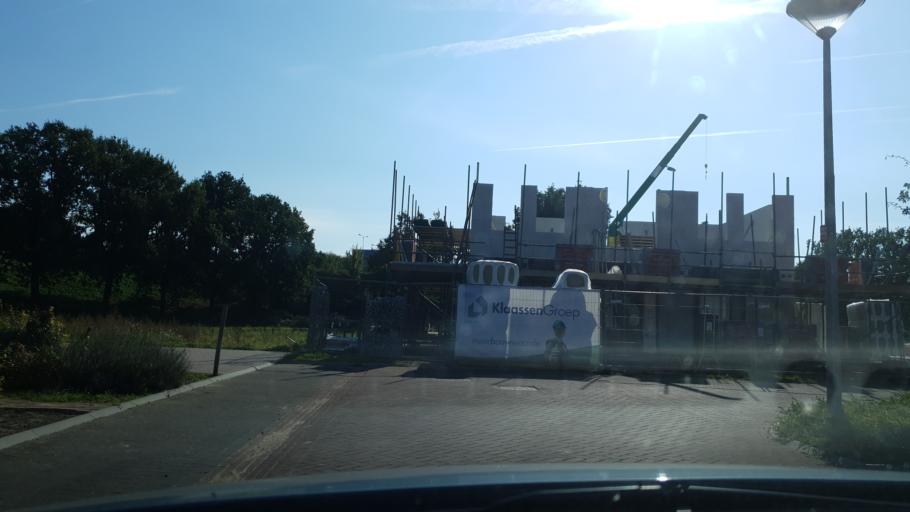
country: NL
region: Gelderland
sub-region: Gemeente Overbetuwe
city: Oosterhout
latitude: 51.8566
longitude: 5.8214
